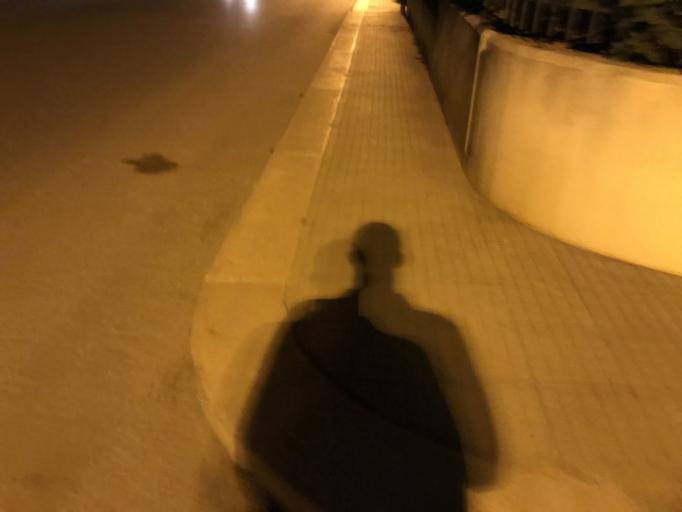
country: IT
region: Apulia
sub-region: Provincia di Bari
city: Corato
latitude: 41.1554
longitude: 16.4018
